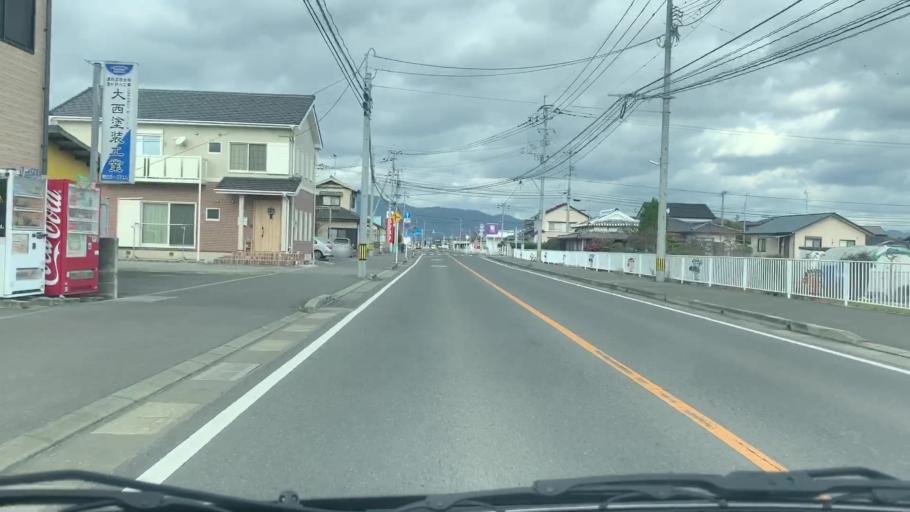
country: JP
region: Saga Prefecture
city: Saga-shi
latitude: 33.2464
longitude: 130.2378
